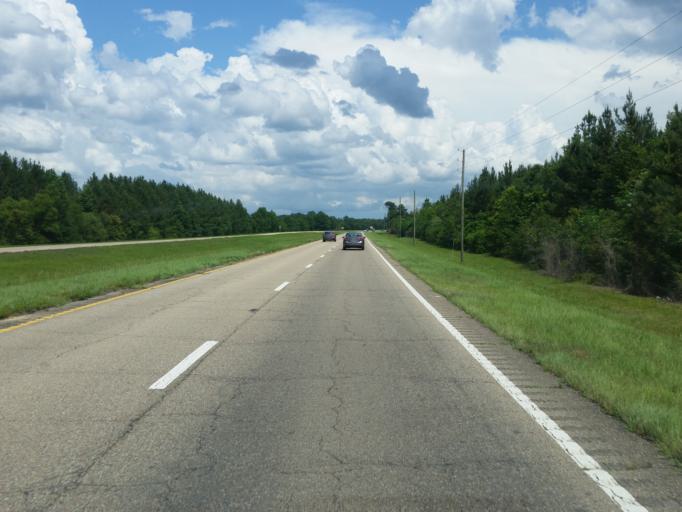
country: US
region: Mississippi
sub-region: Perry County
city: New Augusta
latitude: 31.1438
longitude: -88.8735
